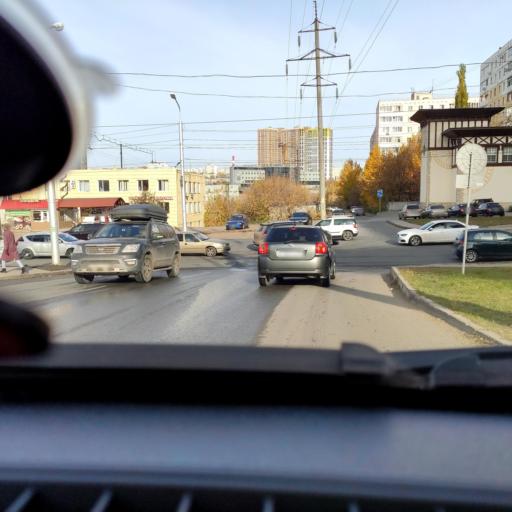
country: RU
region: Bashkortostan
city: Ufa
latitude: 54.7189
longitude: 55.9855
